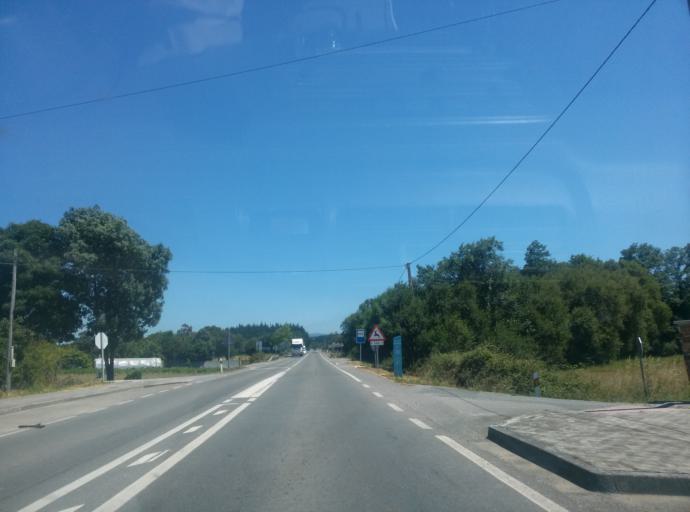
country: ES
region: Galicia
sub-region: Provincia de Lugo
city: Castro de Rei
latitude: 43.2507
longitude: -7.4234
